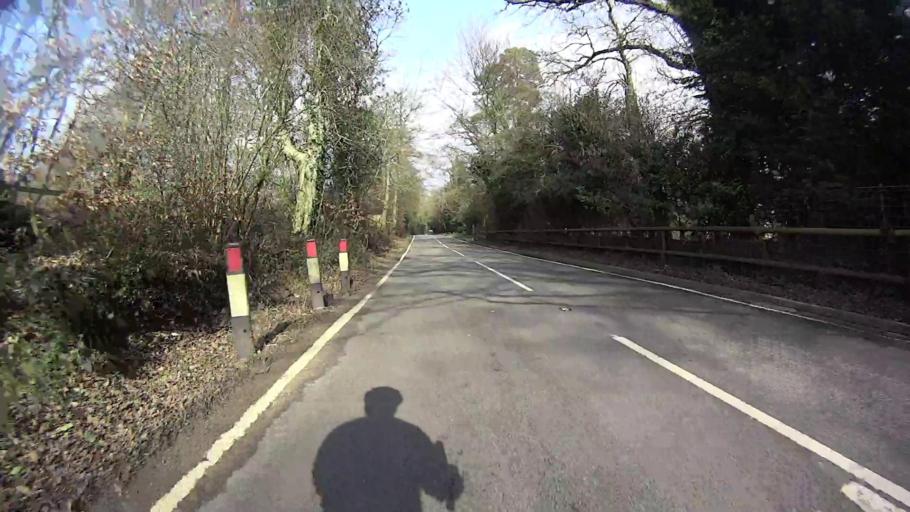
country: GB
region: England
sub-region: Surrey
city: Headley
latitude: 51.2614
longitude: -0.2680
